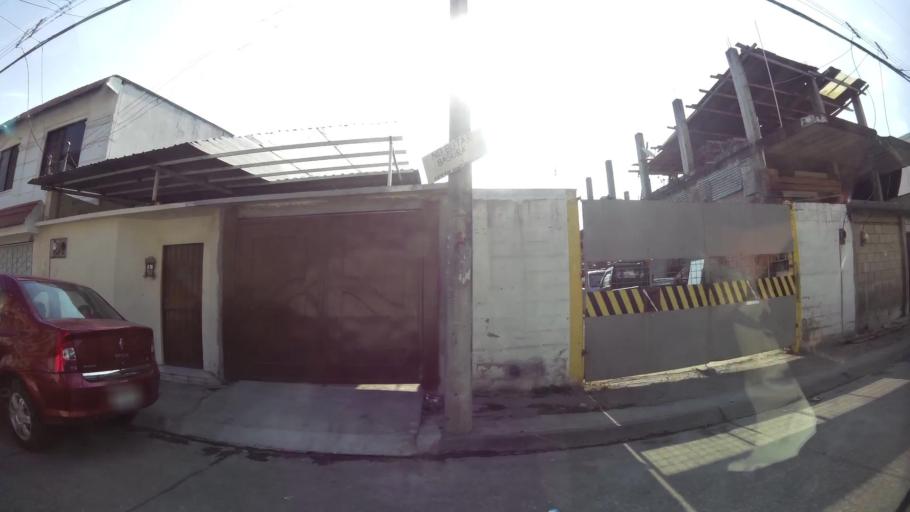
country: EC
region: Guayas
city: Guayaquil
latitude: -2.1507
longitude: -79.9124
